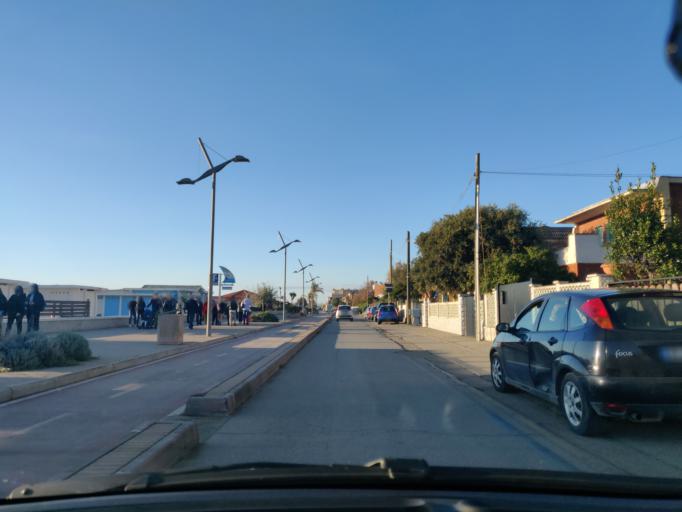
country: IT
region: Latium
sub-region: Provincia di Viterbo
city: Tarquinia
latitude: 42.2185
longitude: 11.7079
